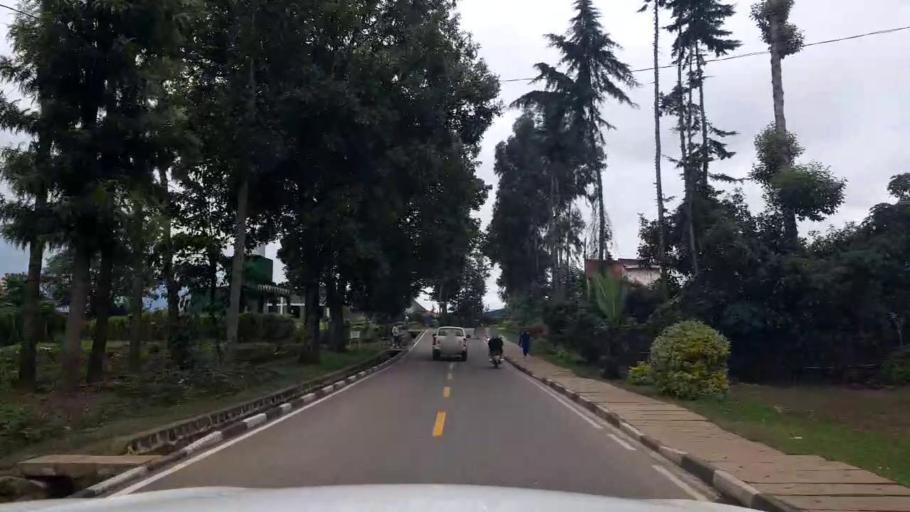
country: RW
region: Northern Province
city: Musanze
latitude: -1.4499
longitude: 29.5915
